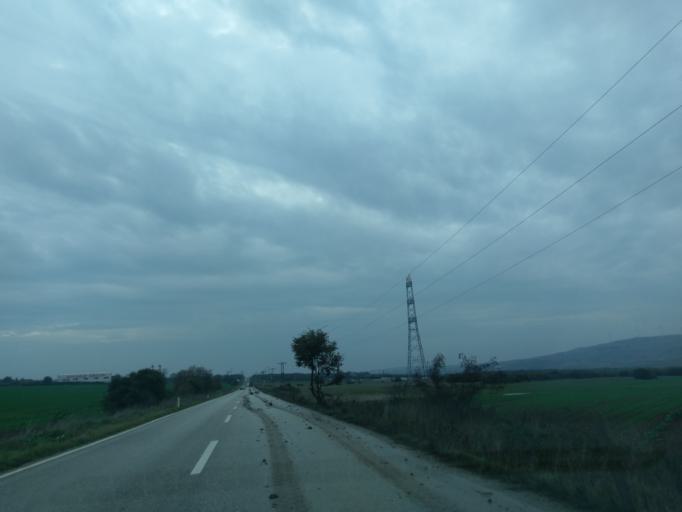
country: TR
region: Istanbul
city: Canta
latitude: 41.1493
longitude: 28.1068
